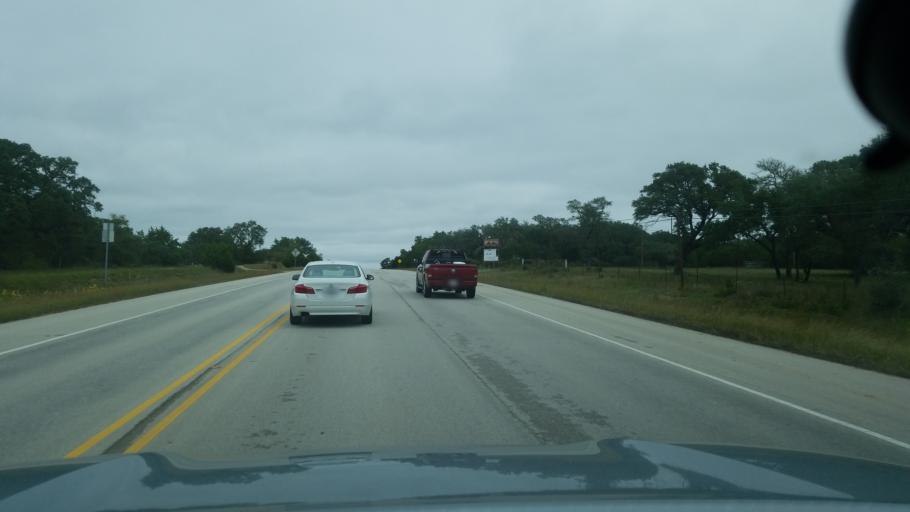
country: US
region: Texas
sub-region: Blanco County
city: Blanco
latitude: 30.0055
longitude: -98.4056
